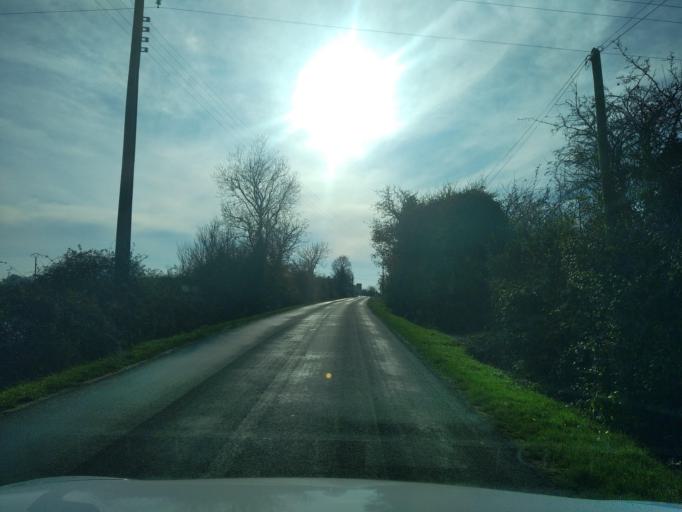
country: FR
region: Pays de la Loire
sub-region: Departement de la Vendee
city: Maillezais
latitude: 46.3643
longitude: -0.7427
